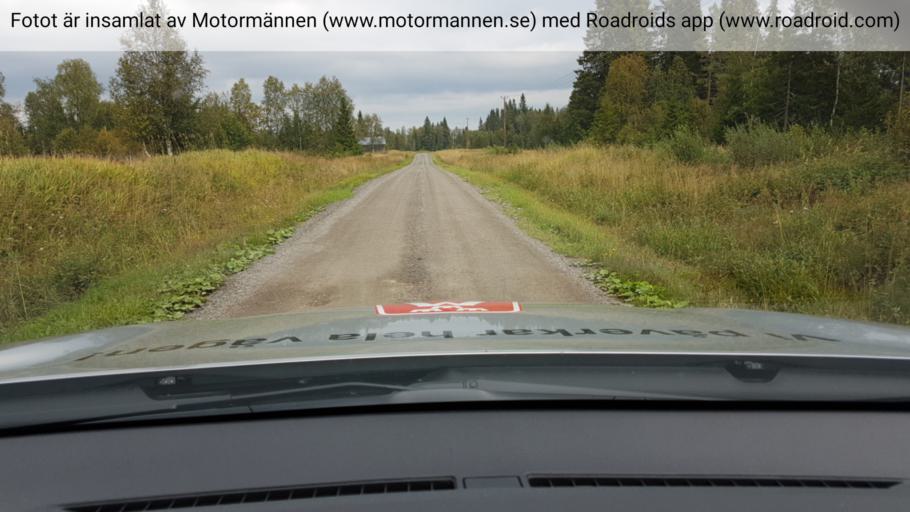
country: SE
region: Jaemtland
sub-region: Stroemsunds Kommun
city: Stroemsund
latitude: 63.7809
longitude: 15.2441
